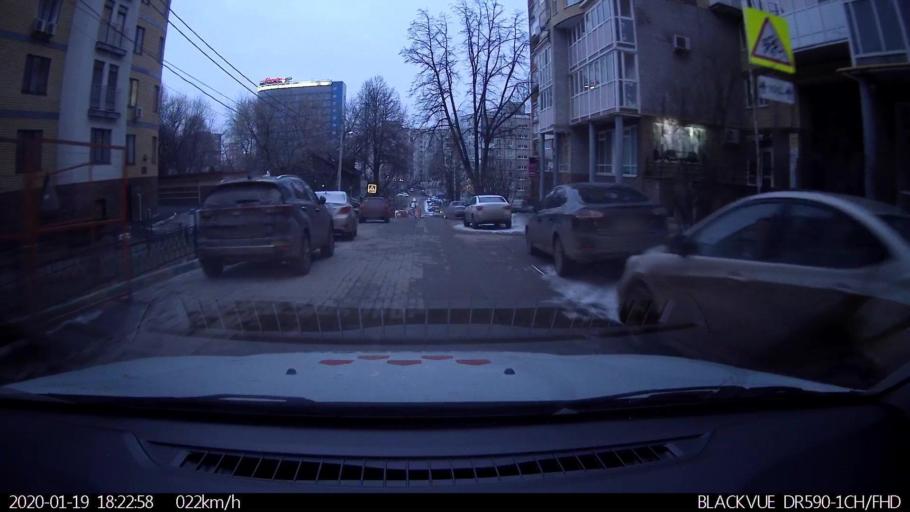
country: RU
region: Nizjnij Novgorod
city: Nizhniy Novgorod
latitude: 56.3227
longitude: 44.0306
